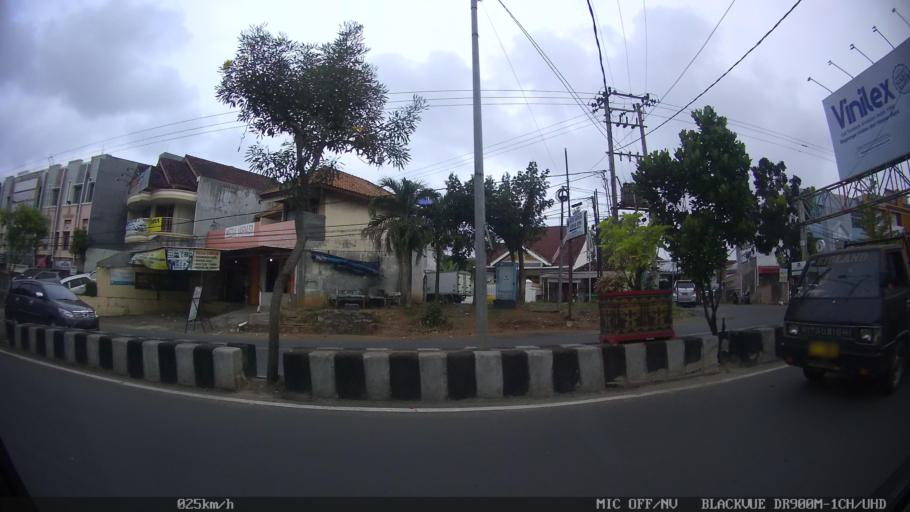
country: ID
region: Lampung
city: Bandarlampung
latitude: -5.4077
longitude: 105.2737
